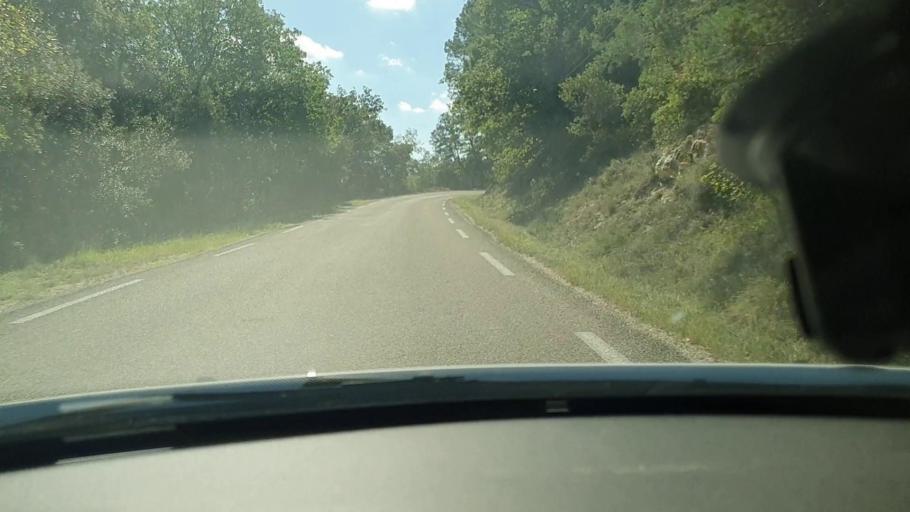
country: FR
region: Languedoc-Roussillon
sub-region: Departement du Gard
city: Goudargues
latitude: 44.1706
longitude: 4.4878
